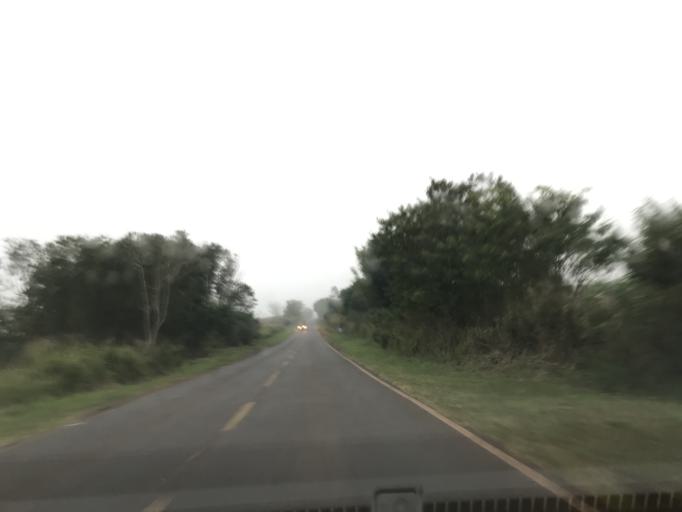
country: PY
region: Canindeyu
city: Salto del Guaira
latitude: -24.1070
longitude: -54.1077
